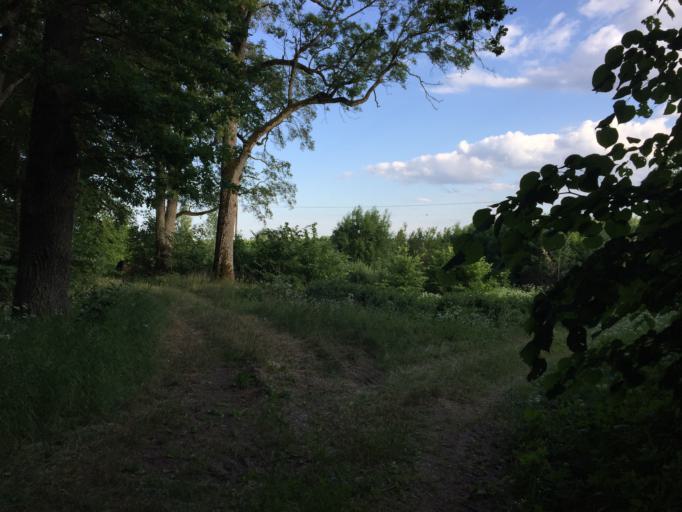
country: LV
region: Skriveri
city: Skriveri
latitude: 56.8342
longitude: 25.2136
